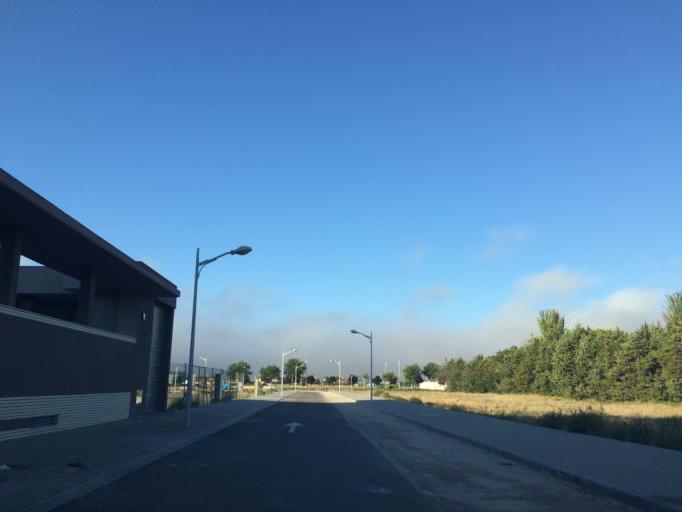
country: ES
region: Castille-La Mancha
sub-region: Provincia de Albacete
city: Albacete
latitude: 39.0056
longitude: -1.8813
